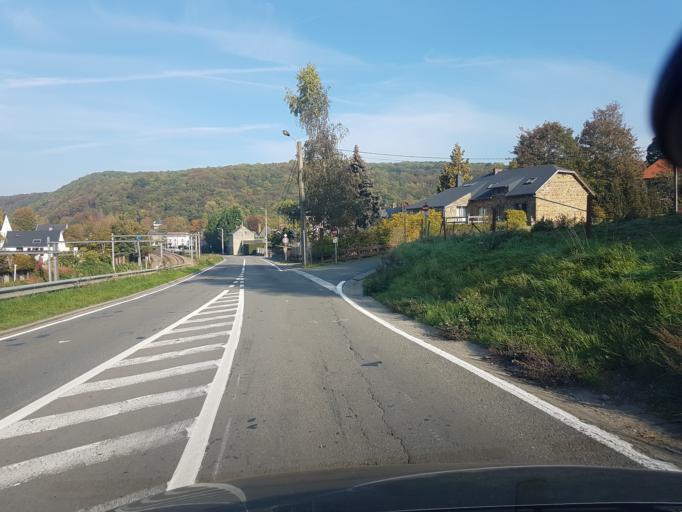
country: BE
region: Wallonia
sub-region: Province de Namur
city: Profondeville
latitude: 50.4129
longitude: 4.8878
